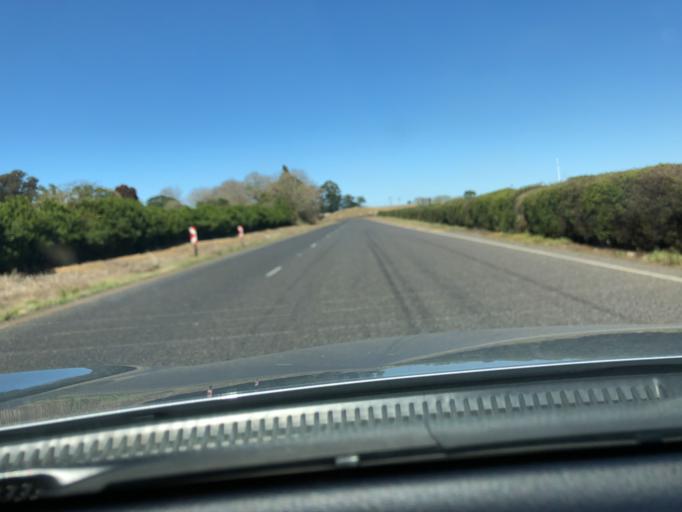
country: ZA
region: KwaZulu-Natal
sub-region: uMgungundlovu District Municipality
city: Howick
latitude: -29.4482
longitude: 30.1782
